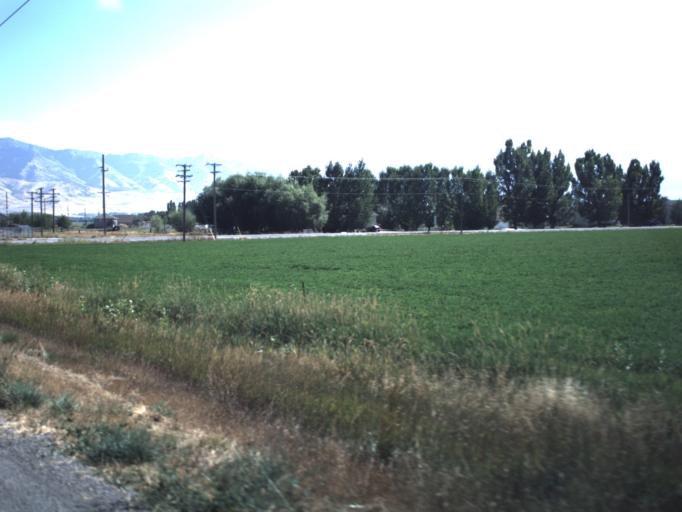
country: US
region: Utah
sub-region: Cache County
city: Smithfield
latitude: 41.8453
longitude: -111.8952
